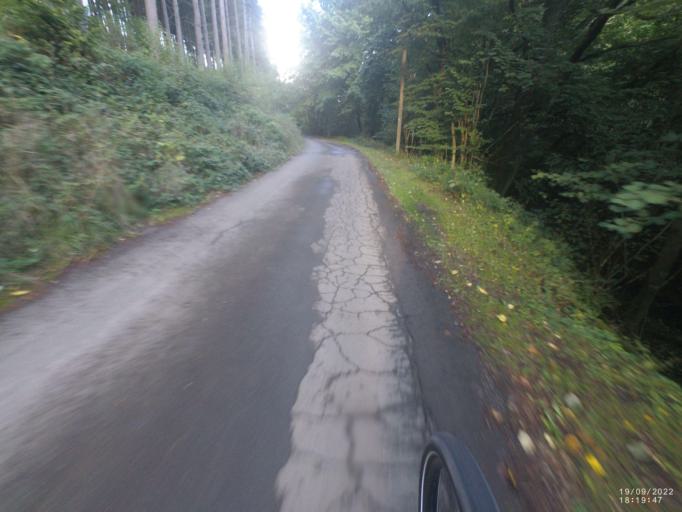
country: DE
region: Rheinland-Pfalz
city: Schalkenmehren
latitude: 50.1513
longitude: 6.8290
